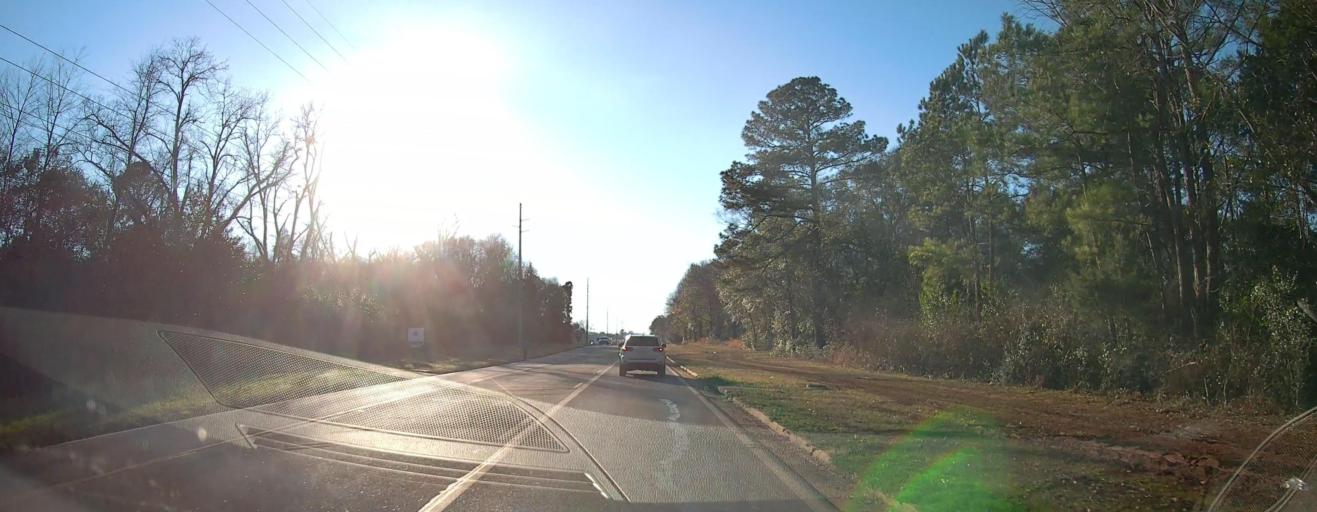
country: US
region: Georgia
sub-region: Dougherty County
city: Albany
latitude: 31.6231
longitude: -84.1809
